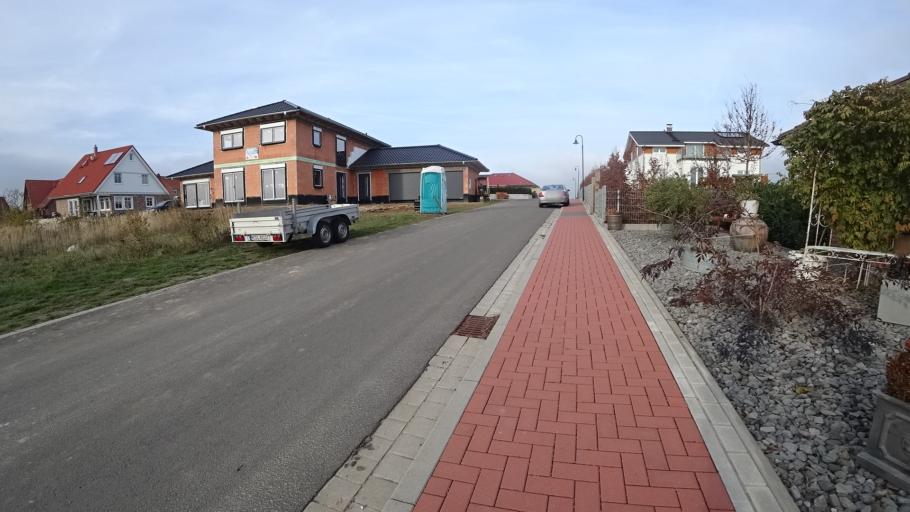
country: DE
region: Lower Saxony
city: Lauenau
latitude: 52.2786
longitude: 9.3790
